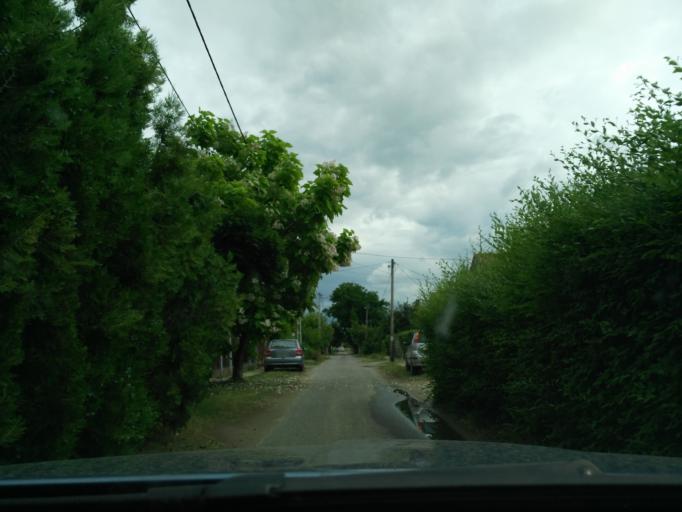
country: HU
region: Hajdu-Bihar
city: Debrecen
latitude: 47.5501
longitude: 21.6557
